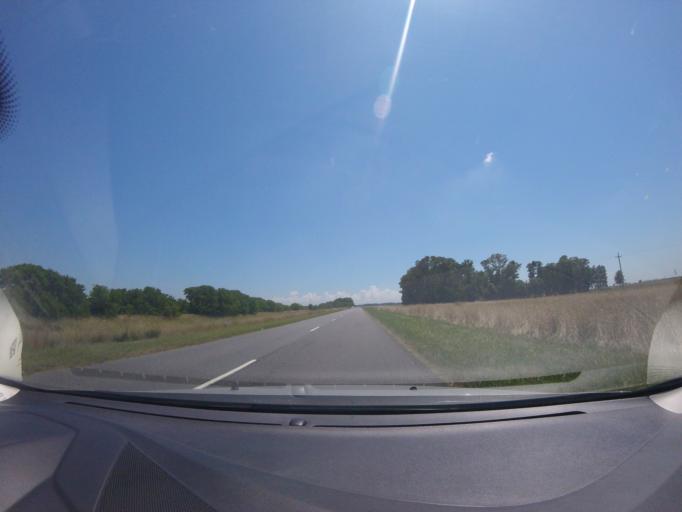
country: AR
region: Buenos Aires
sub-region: Partido de Rauch
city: Rauch
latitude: -36.4527
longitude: -59.0141
